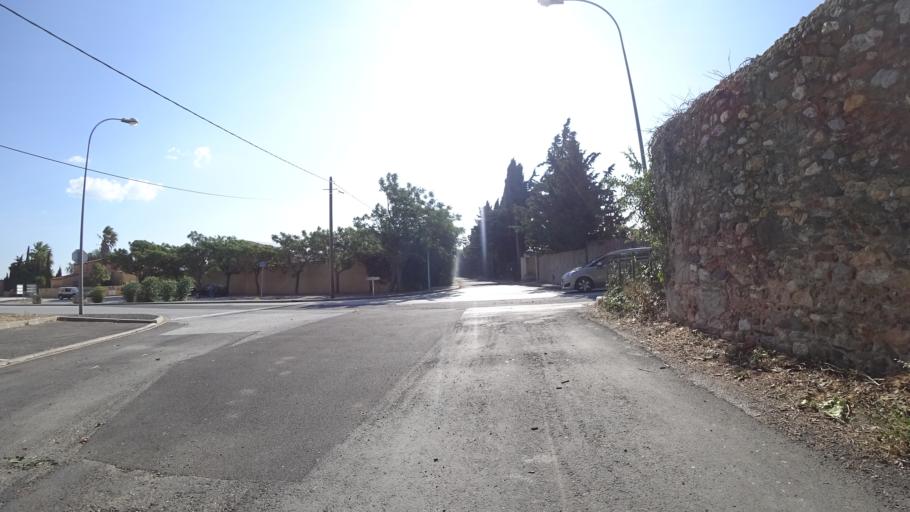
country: FR
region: Languedoc-Roussillon
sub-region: Departement des Pyrenees-Orientales
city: Rivesaltes
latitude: 42.7747
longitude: 2.8797
